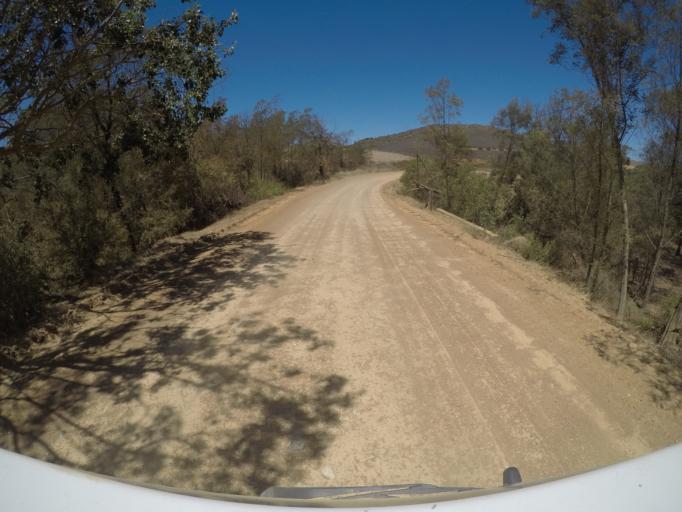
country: ZA
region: Western Cape
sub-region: Overberg District Municipality
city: Caledon
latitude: -34.1455
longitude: 19.2474
